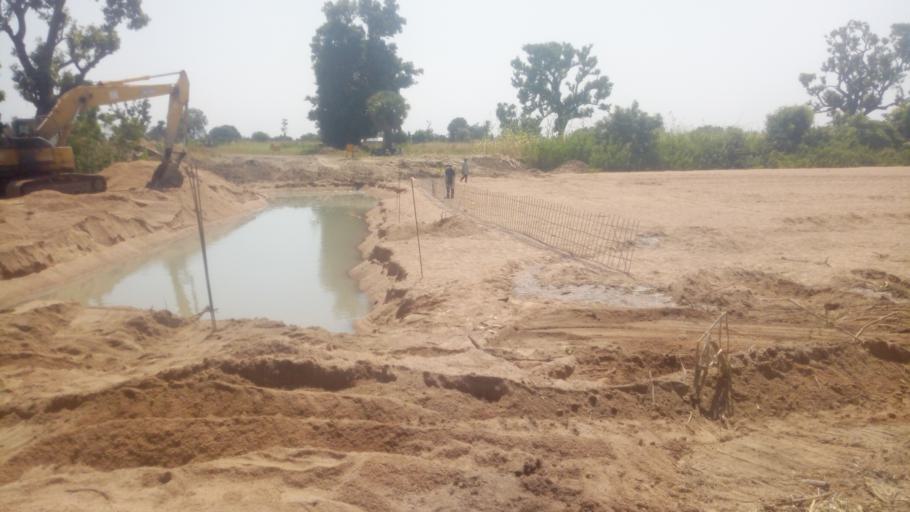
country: NG
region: Adamawa
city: Mayo Belwa
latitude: 9.1577
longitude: 12.0151
